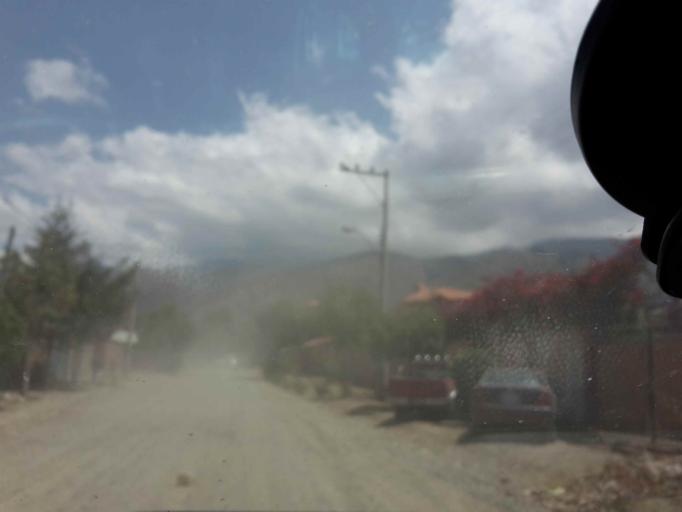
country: BO
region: Cochabamba
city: Cochabamba
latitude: -17.3337
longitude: -66.2189
